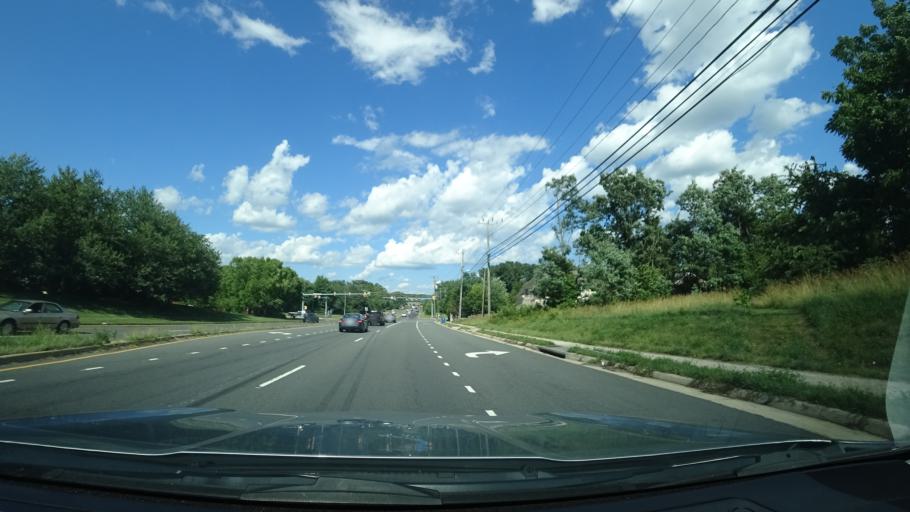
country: US
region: Virginia
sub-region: Loudoun County
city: Sterling
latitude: 39.0066
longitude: -77.4234
